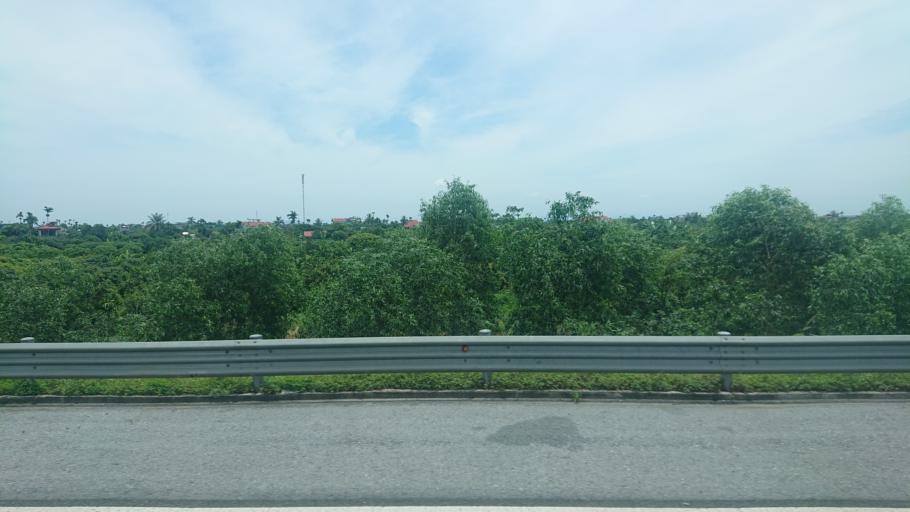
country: VN
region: Hai Duong
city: Tu Ky
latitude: 20.8200
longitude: 106.4793
